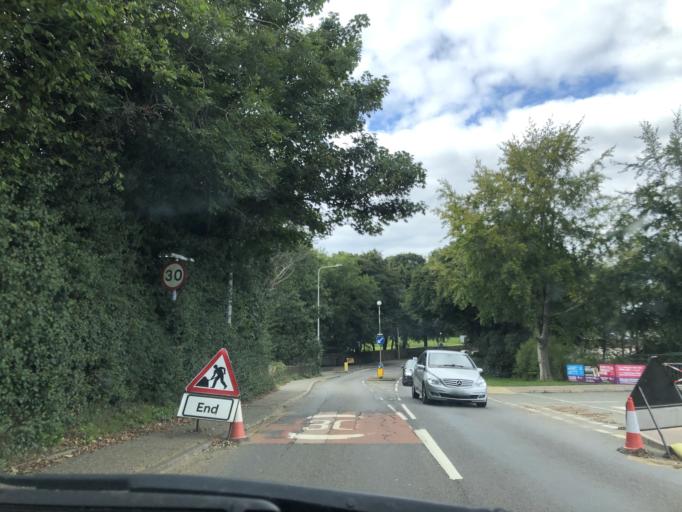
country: GB
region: England
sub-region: Kent
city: Sevenoaks
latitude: 51.2631
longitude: 0.1946
